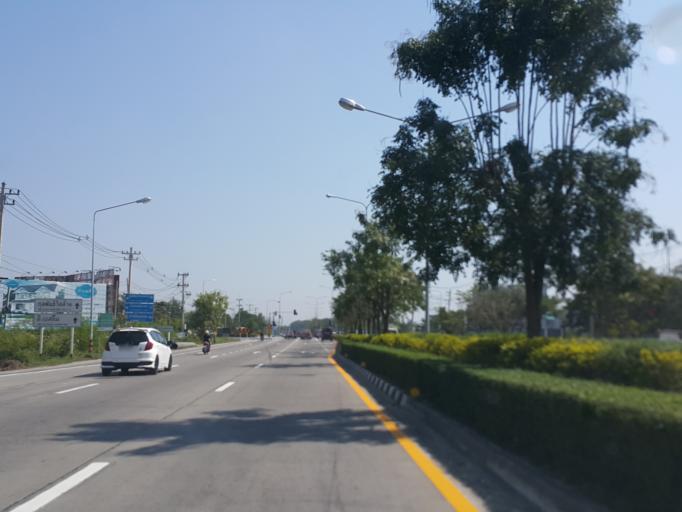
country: TH
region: Chiang Mai
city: Saraphi
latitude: 18.7643
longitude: 99.0374
